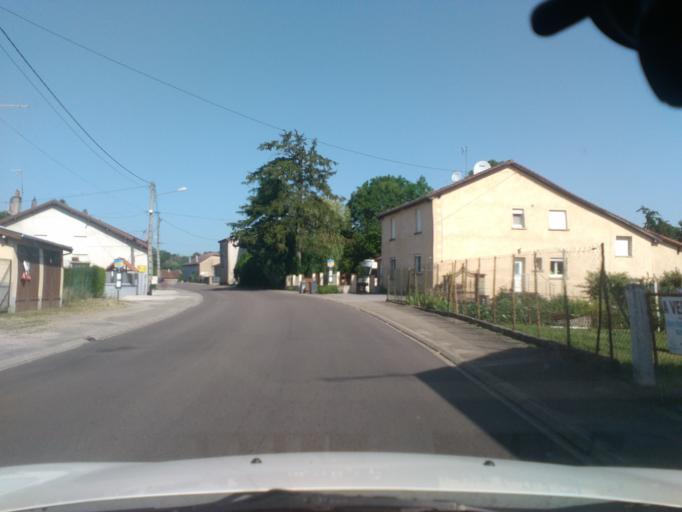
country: FR
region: Lorraine
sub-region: Departement des Vosges
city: Mirecourt
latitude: 48.3098
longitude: 6.1007
